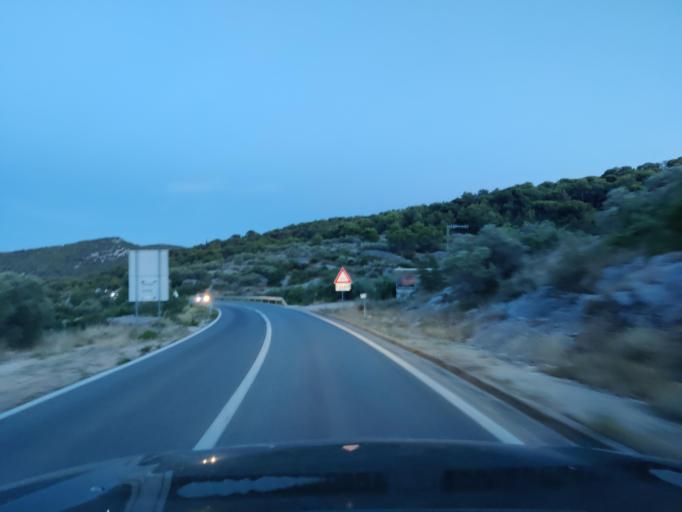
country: HR
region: Sibensko-Kniniska
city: Murter
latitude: 43.8104
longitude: 15.6025
